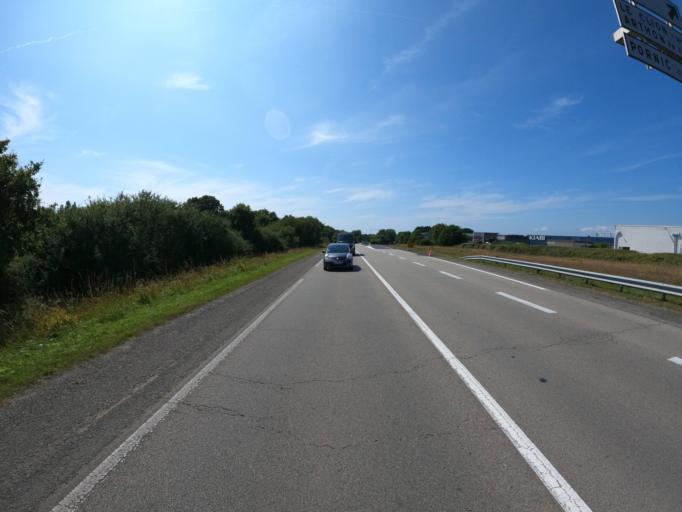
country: FR
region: Pays de la Loire
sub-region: Departement de la Loire-Atlantique
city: Pornic
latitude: 47.1094
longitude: -2.0695
